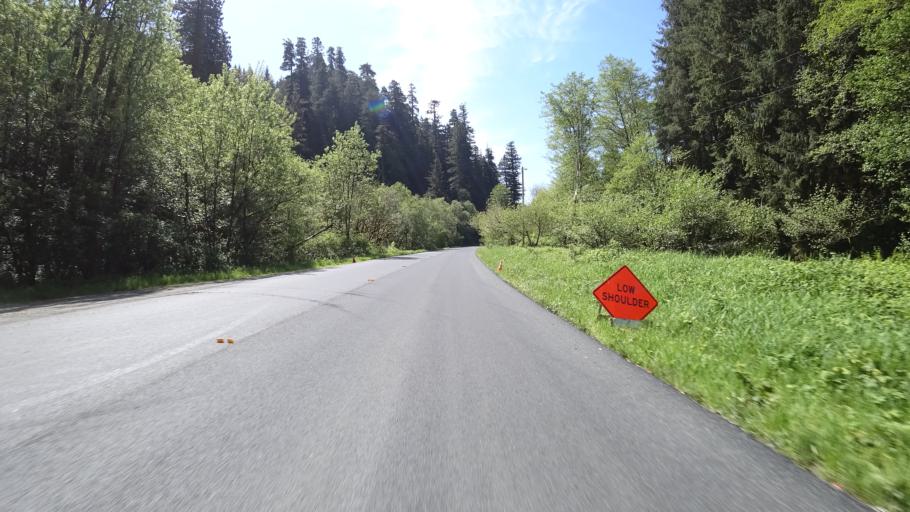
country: US
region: California
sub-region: Humboldt County
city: Westhaven-Moonstone
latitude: 41.3369
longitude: -124.0306
